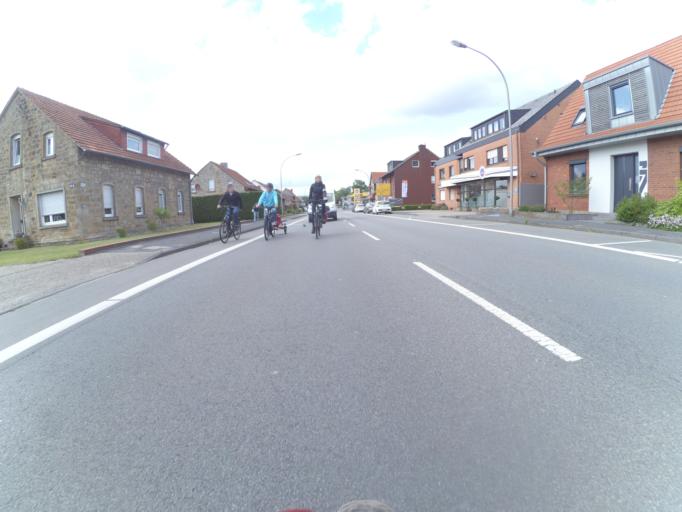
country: DE
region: North Rhine-Westphalia
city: Ibbenburen
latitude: 52.2648
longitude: 7.7157
